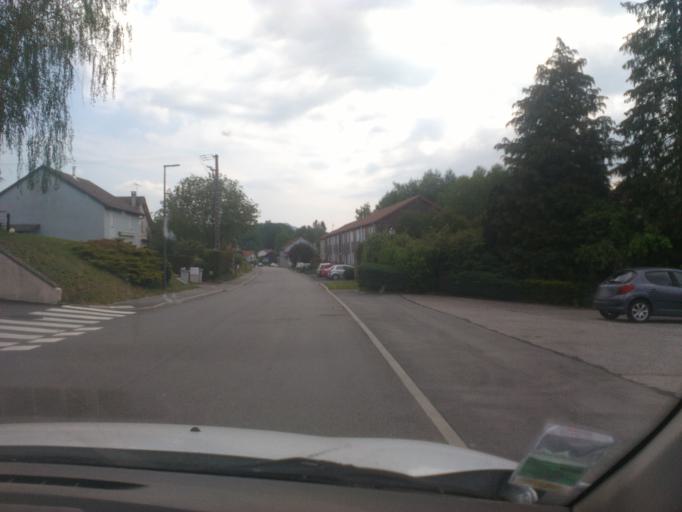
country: FR
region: Lorraine
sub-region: Departement des Vosges
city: Etival-Clairefontaine
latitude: 48.3606
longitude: 6.8456
